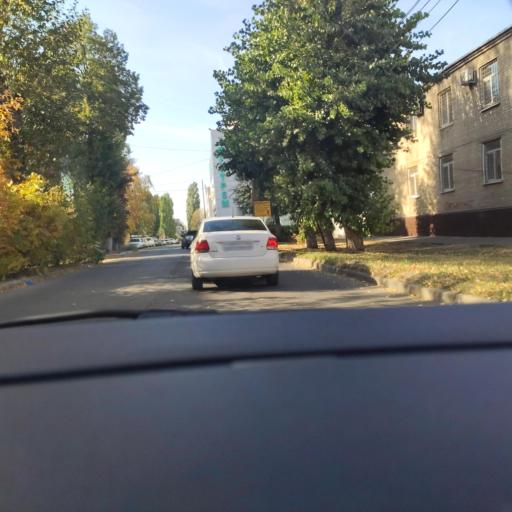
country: RU
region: Voronezj
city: Voronezh
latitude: 51.6791
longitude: 39.1557
